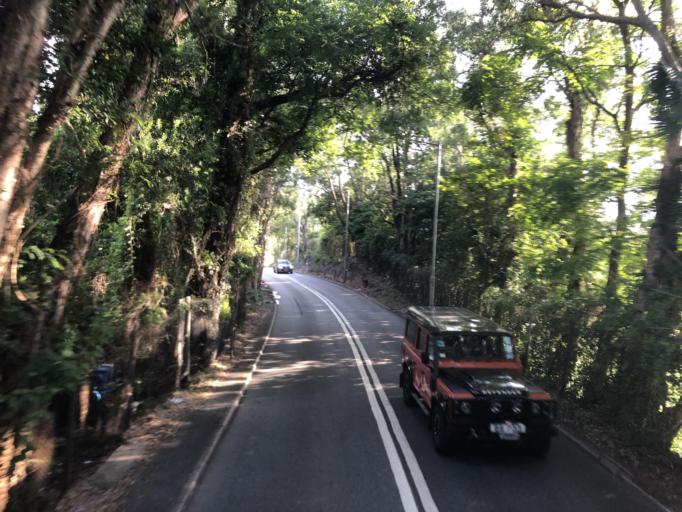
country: HK
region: Tai Po
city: Tai Po
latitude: 22.4939
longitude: 114.1201
